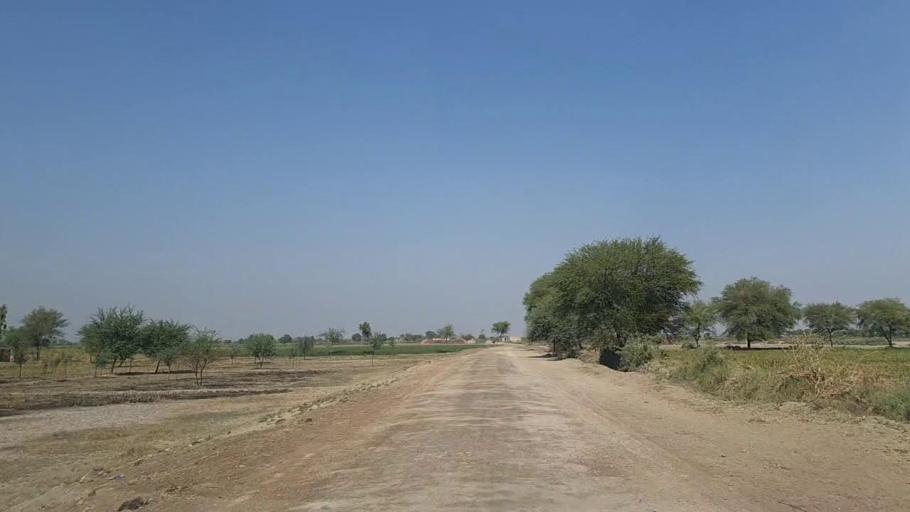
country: PK
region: Sindh
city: Samaro
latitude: 25.2152
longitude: 69.4043
